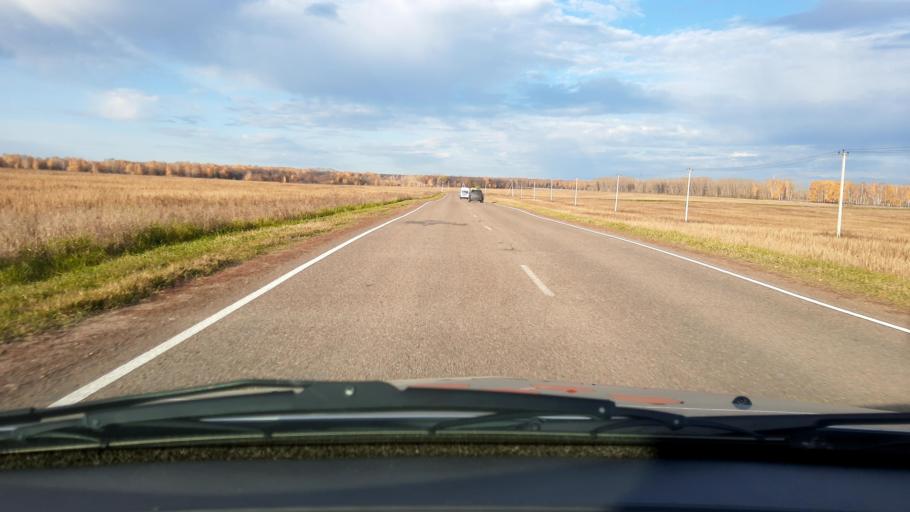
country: RU
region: Bashkortostan
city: Mikhaylovka
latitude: 54.8174
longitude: 55.7747
